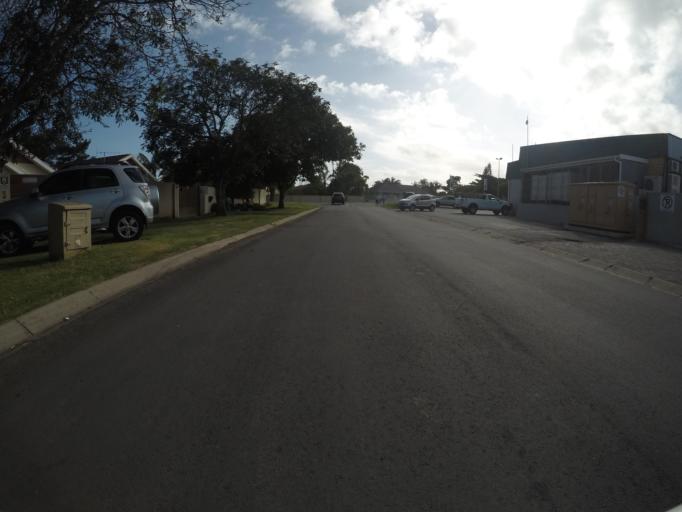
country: ZA
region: Eastern Cape
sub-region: Buffalo City Metropolitan Municipality
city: East London
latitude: -32.9697
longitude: 27.9510
